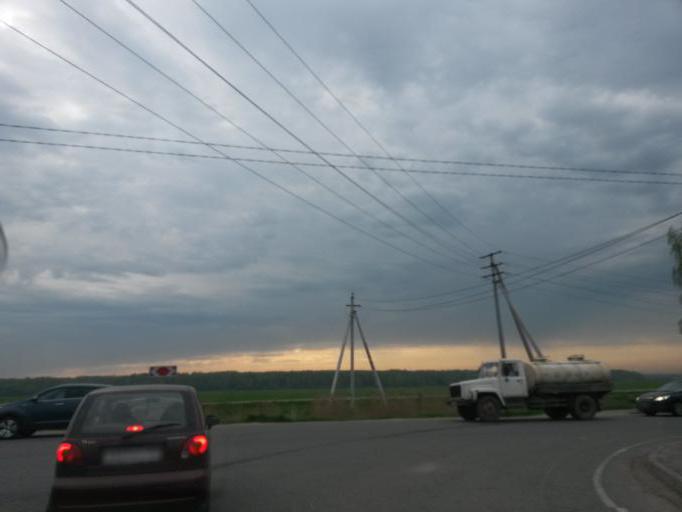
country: RU
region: Moskovskaya
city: Barybino
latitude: 55.2035
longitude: 37.8690
